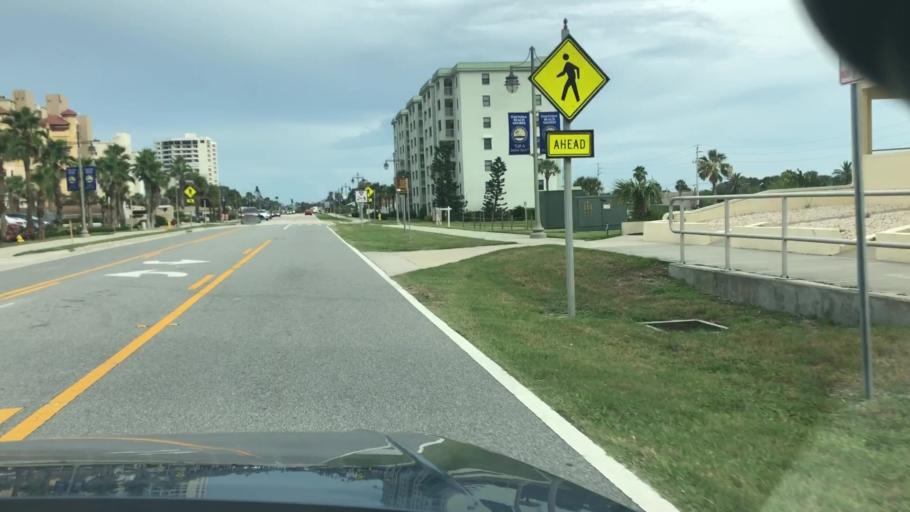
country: US
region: Florida
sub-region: Volusia County
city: Port Orange
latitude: 29.1419
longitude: -80.9641
